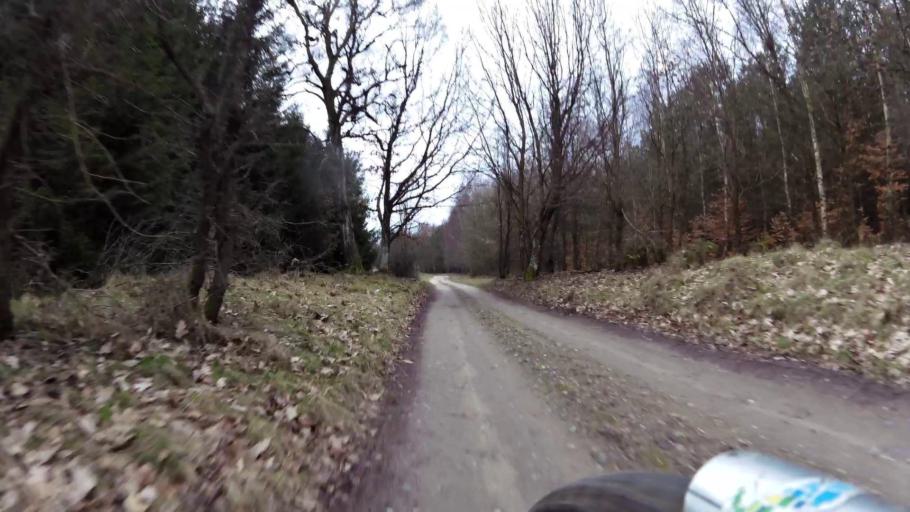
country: PL
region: Pomeranian Voivodeship
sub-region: Powiat bytowski
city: Trzebielino
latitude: 54.1122
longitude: 17.1295
